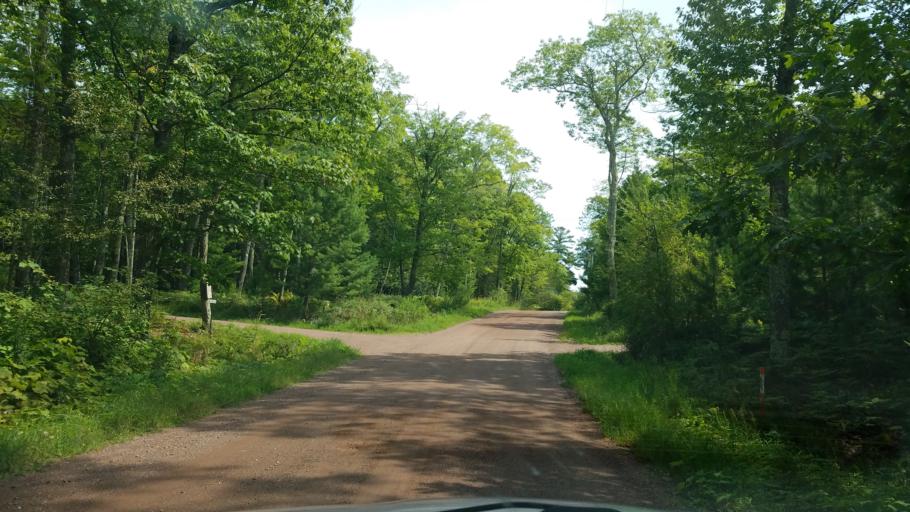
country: US
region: Wisconsin
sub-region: Bayfield County
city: Washburn
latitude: 46.7537
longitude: -90.7796
